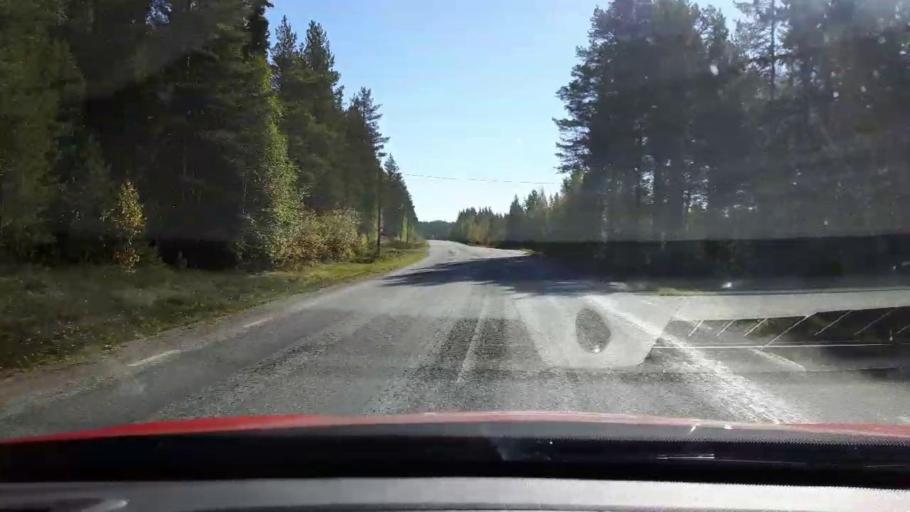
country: SE
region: Jaemtland
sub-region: Harjedalens Kommun
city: Sveg
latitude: 62.3393
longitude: 14.0413
